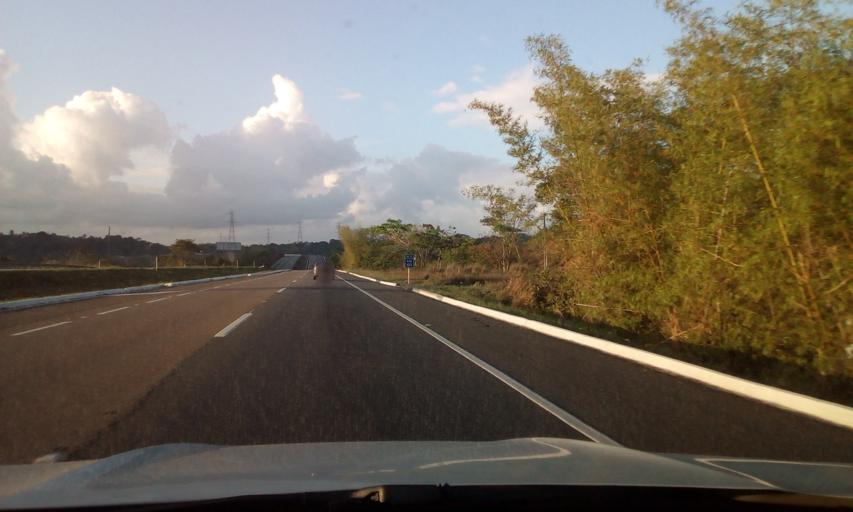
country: BR
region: Paraiba
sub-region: Conde
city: Conde
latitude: -7.3079
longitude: -34.9433
